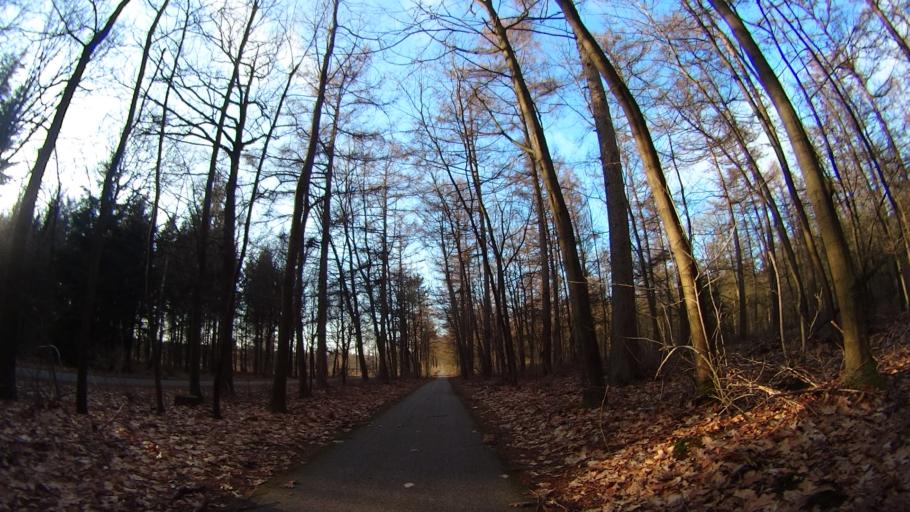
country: NL
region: Drenthe
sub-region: Gemeente Coevorden
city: Sleen
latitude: 52.8239
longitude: 6.7603
